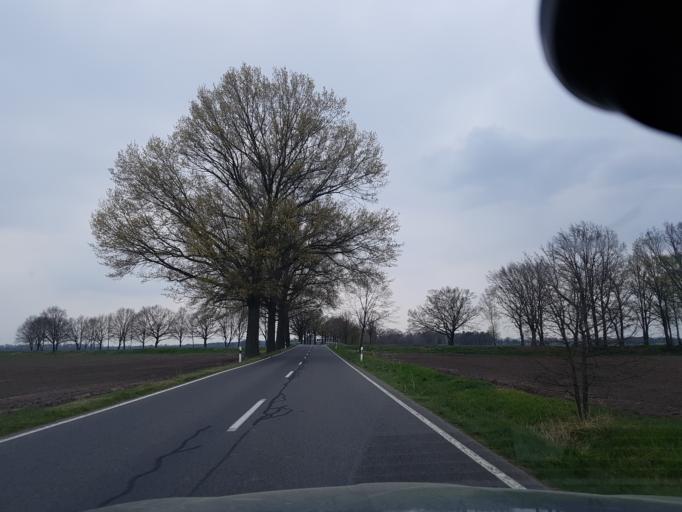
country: DE
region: Brandenburg
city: Schraden
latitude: 51.4025
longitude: 13.7002
